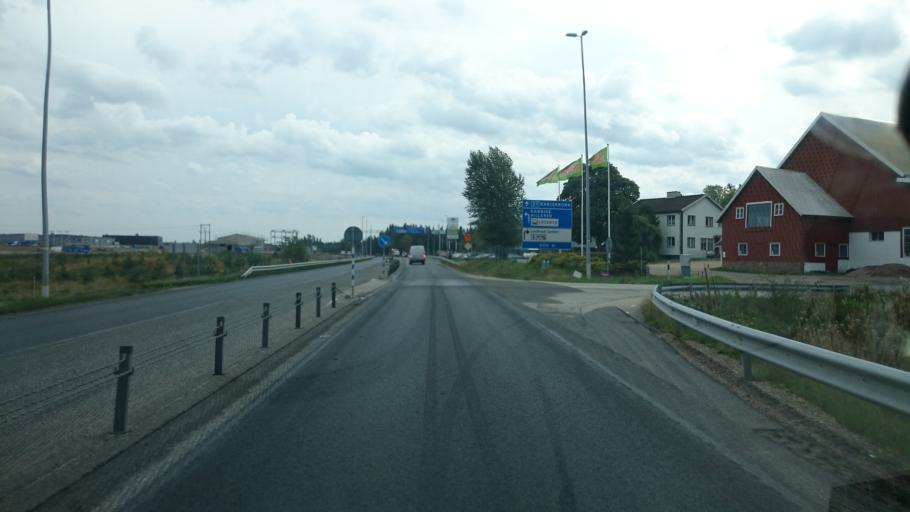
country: SE
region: Vaestra Goetaland
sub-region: Boras Kommun
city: Dalsjofors
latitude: 57.6173
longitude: 13.1101
